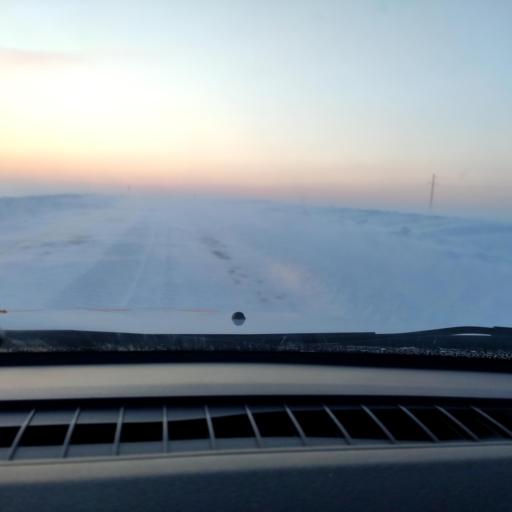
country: RU
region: Samara
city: Georgiyevka
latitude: 53.4167
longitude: 50.8962
